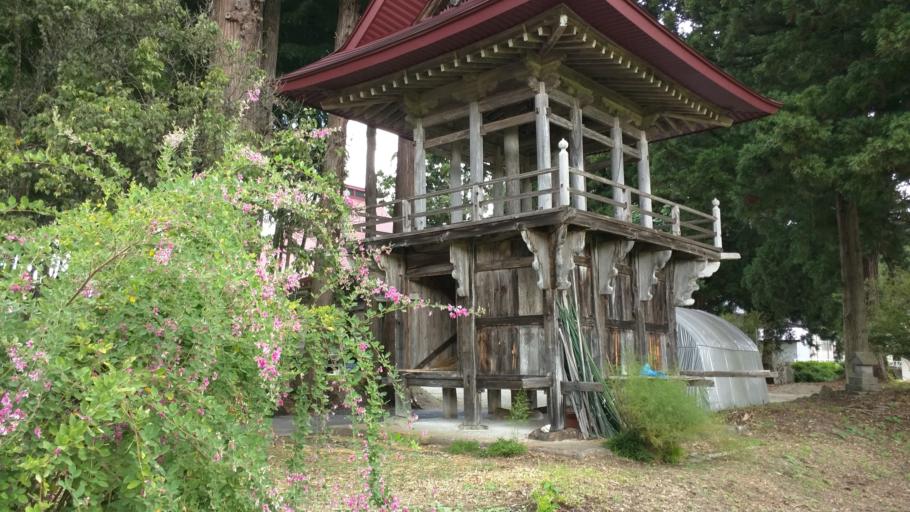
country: JP
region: Fukushima
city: Kitakata
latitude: 37.4311
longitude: 139.8085
